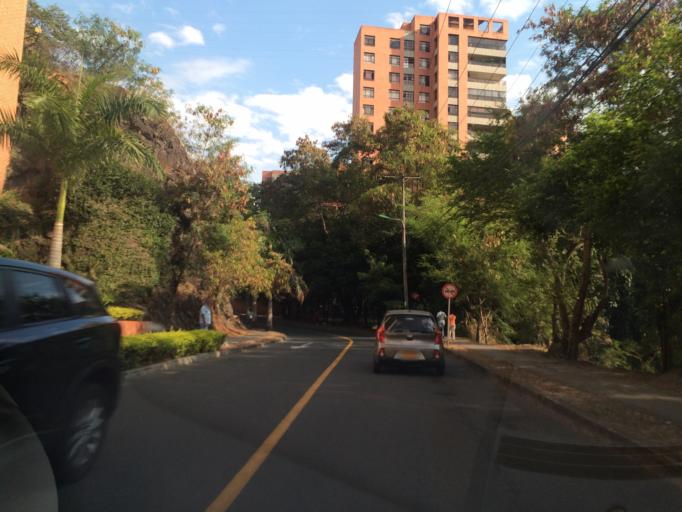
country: CO
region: Valle del Cauca
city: Cali
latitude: 3.4551
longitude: -76.5490
